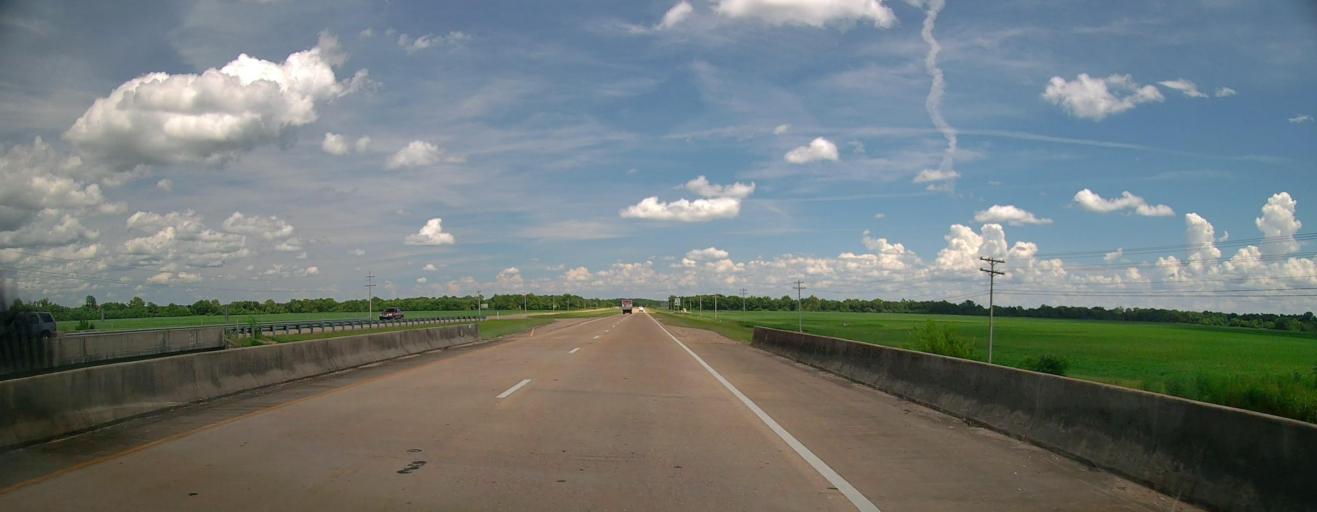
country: US
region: Mississippi
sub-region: Lee County
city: Nettleton
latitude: 34.1036
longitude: -88.6652
